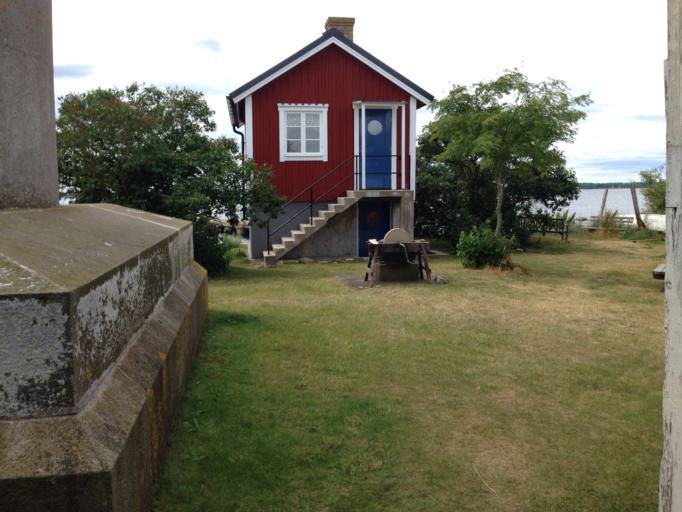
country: SE
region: Kalmar
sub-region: Torsas Kommun
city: Torsas
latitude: 56.3905
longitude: 16.1289
